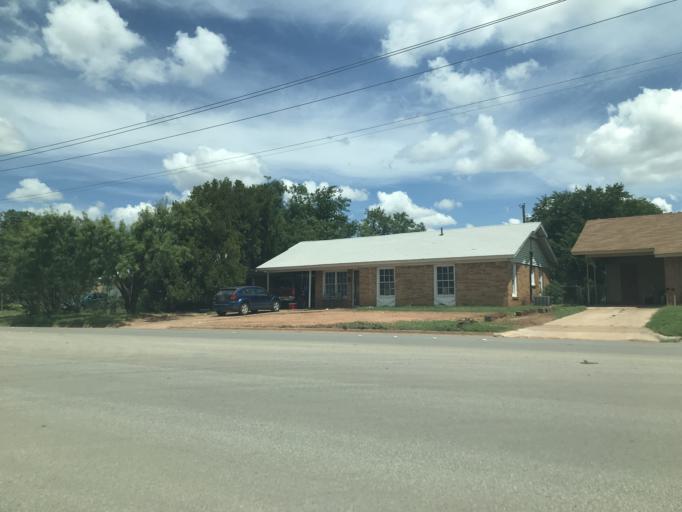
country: US
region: Texas
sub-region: Taylor County
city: Abilene
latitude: 32.4744
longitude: -99.7600
